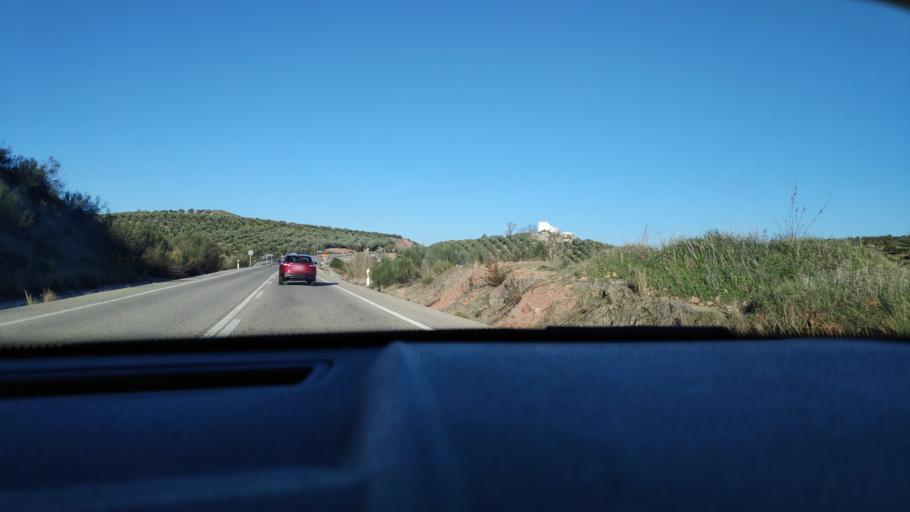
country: ES
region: Andalusia
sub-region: Provincia de Jaen
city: Alcaudete
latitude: 37.6370
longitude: -4.0930
